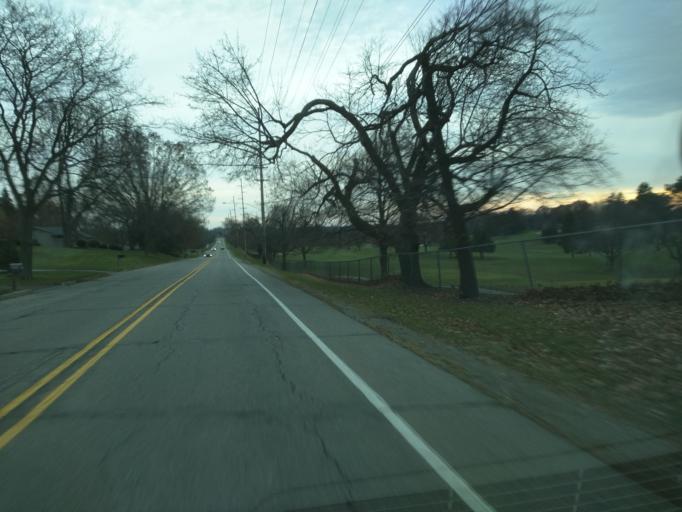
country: US
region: Michigan
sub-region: Ingham County
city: Lansing
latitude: 42.7515
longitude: -84.5232
